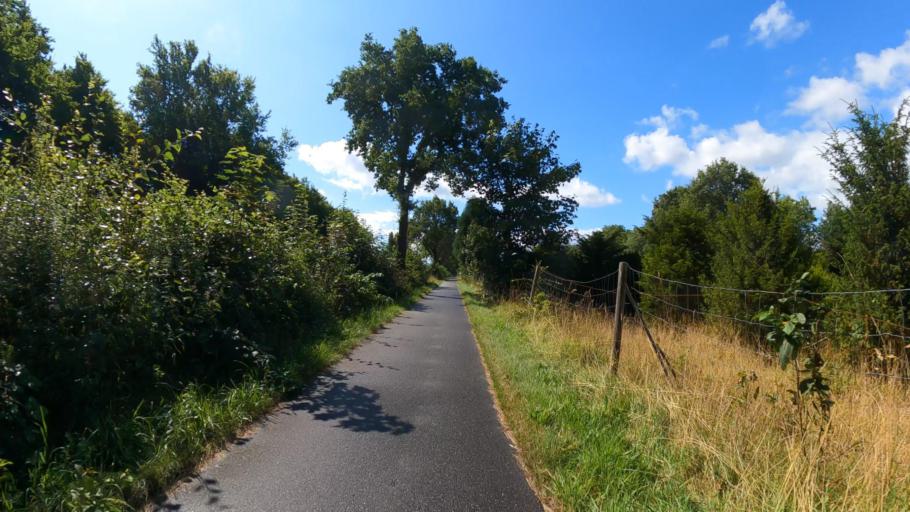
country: DE
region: Schleswig-Holstein
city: Fuhlendorf
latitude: 53.9385
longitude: 9.8939
